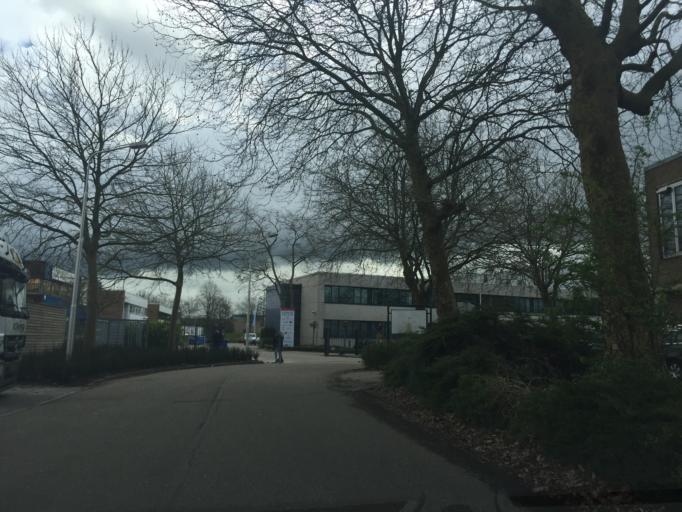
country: NL
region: North Holland
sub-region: Gemeente Aalsmeer
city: Aalsmeer
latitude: 52.2568
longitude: 4.7796
